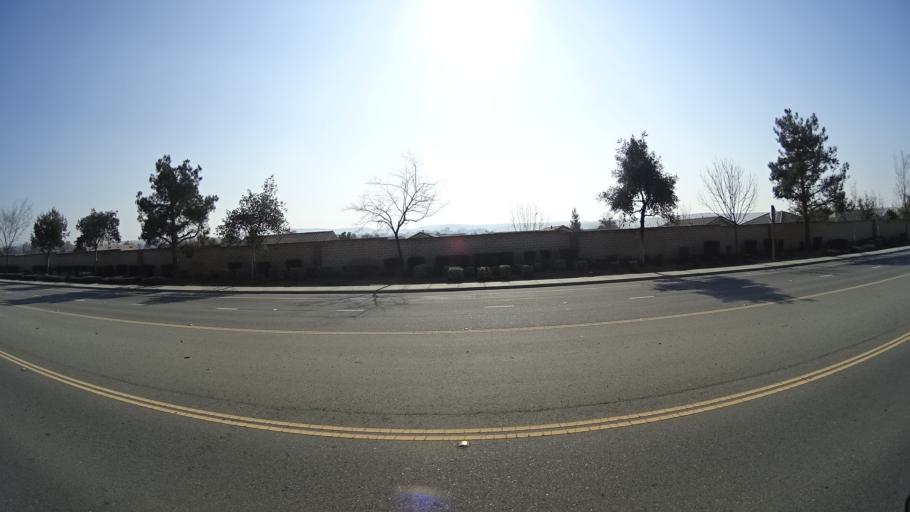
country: US
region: California
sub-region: Kern County
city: Lamont
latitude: 35.4113
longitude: -118.8485
